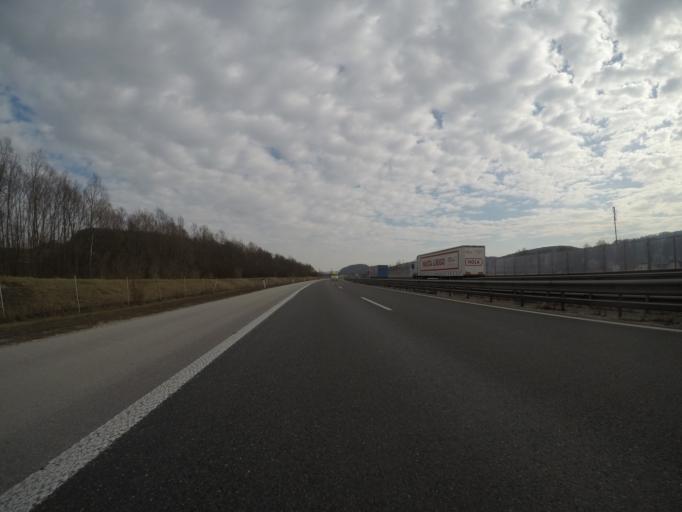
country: SI
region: Pesnica
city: Pesnica pri Mariboru
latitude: 46.5815
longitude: 15.7306
